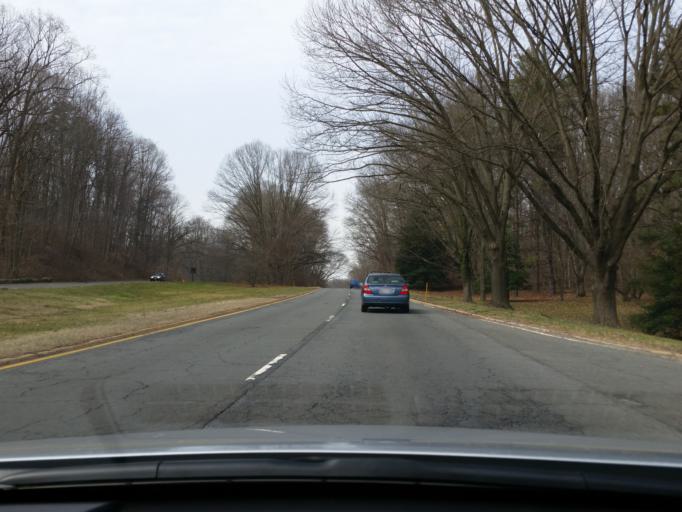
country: US
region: Maryland
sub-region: Montgomery County
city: Cabin John
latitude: 38.9608
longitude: -77.1484
